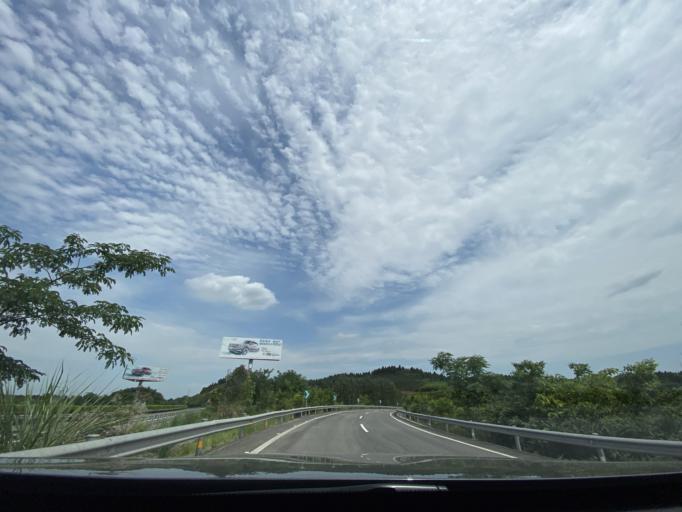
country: CN
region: Sichuan
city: Mianyang
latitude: 31.3510
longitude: 104.7053
